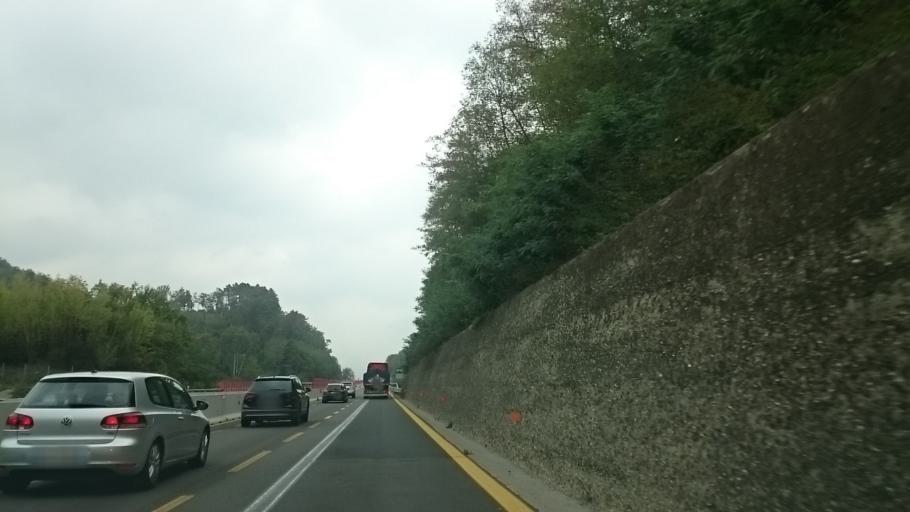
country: IT
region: Tuscany
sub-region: Province of Florence
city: Barberino di Mugello
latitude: 44.0134
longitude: 11.2218
